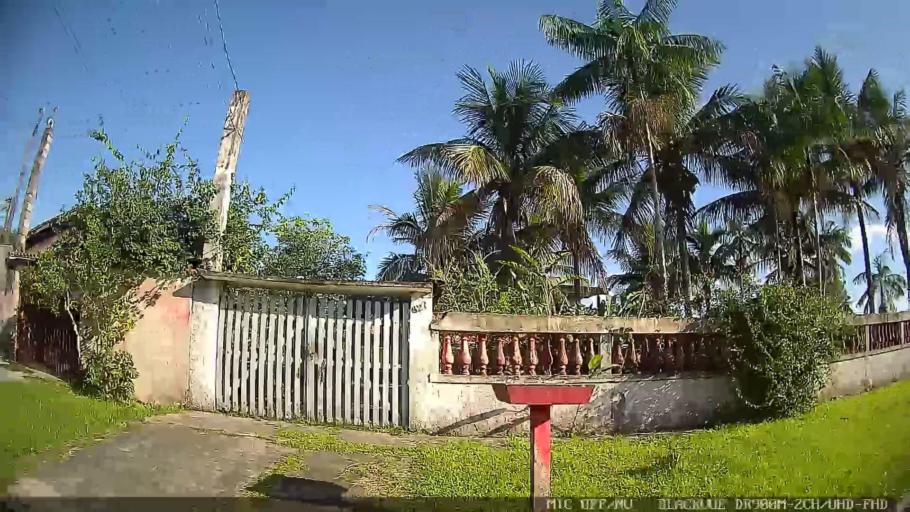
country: BR
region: Sao Paulo
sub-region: Peruibe
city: Peruibe
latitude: -24.2710
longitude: -46.9471
